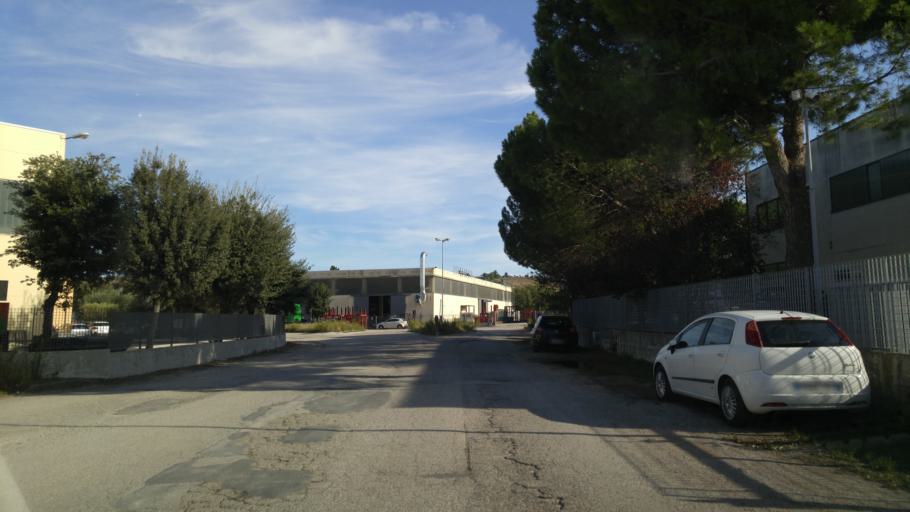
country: IT
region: The Marches
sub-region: Provincia di Pesaro e Urbino
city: Bellocchi
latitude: 43.7853
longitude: 13.0060
